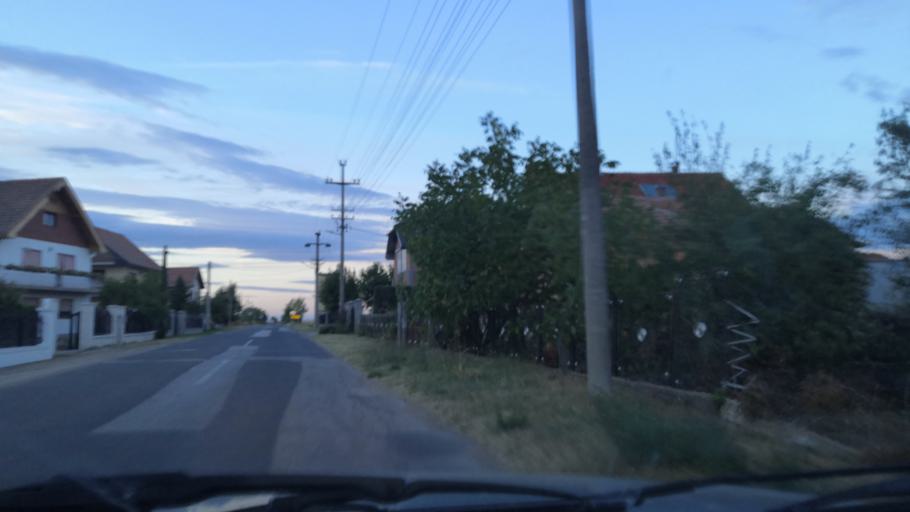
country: RS
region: Central Serbia
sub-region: Borski Okrug
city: Negotin
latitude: 44.2719
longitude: 22.5555
